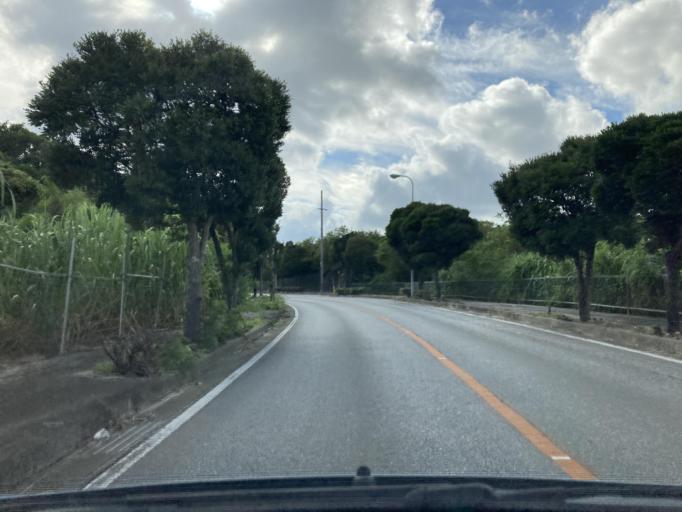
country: JP
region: Okinawa
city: Itoman
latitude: 26.1333
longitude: 127.7065
